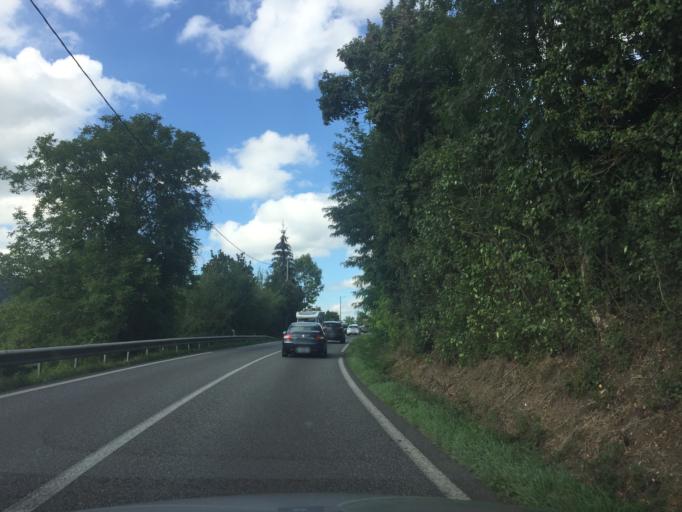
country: FR
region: Midi-Pyrenees
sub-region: Departement de la Haute-Garonne
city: Gourdan-Polignan
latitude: 43.0459
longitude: 0.5912
